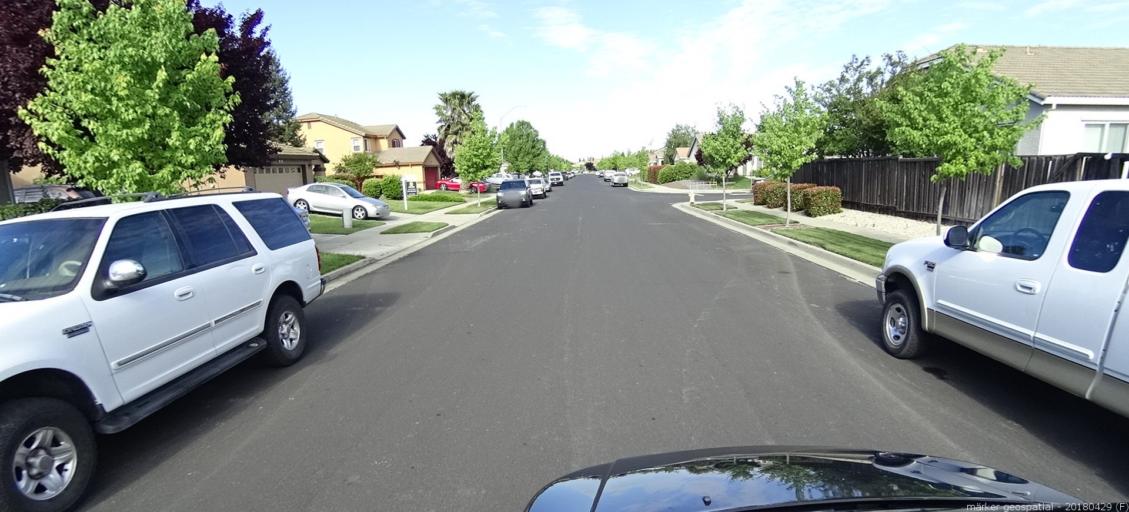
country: US
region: California
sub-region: Yolo County
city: West Sacramento
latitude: 38.5372
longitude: -121.5599
